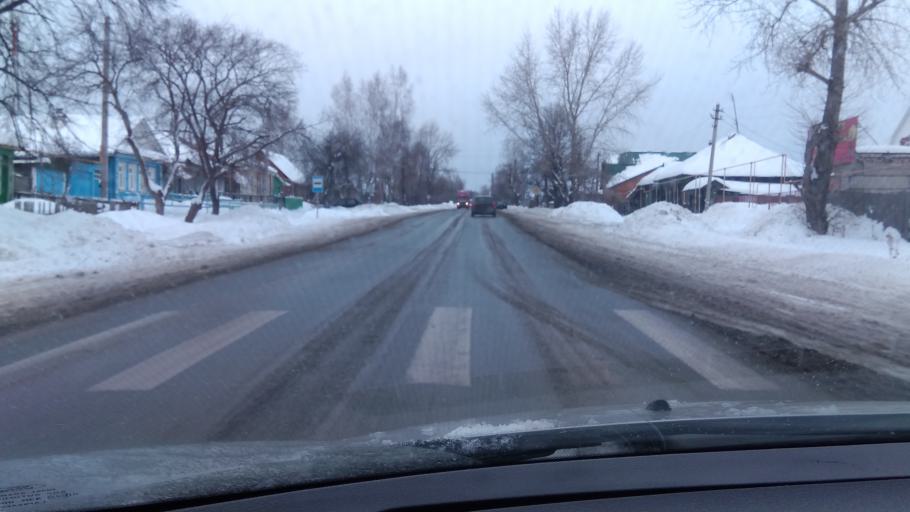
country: RU
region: Sverdlovsk
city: Nikolo-Pavlovskoye
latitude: 57.7879
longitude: 60.0554
